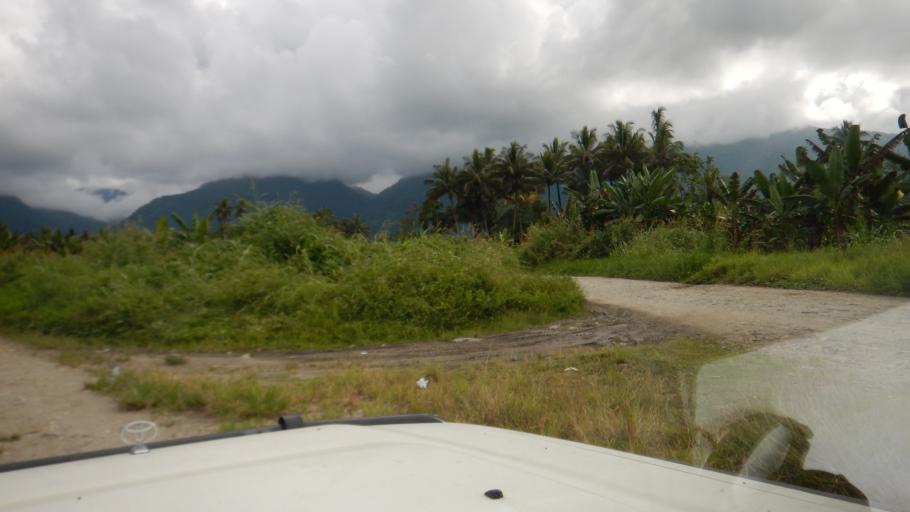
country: PG
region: Northern Province
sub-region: Sohe
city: Kokoda
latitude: -8.8767
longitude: 147.7363
